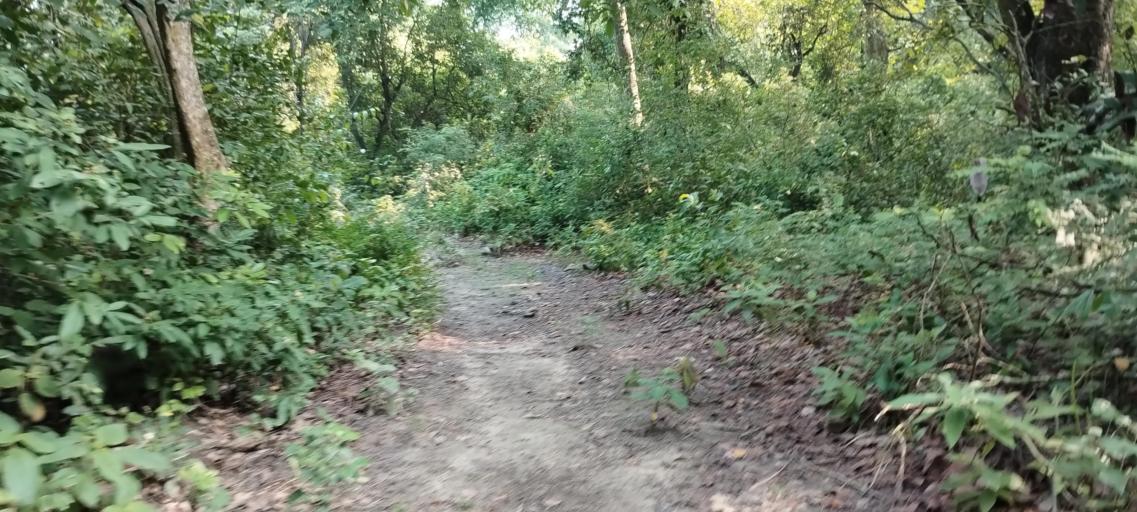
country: NP
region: Far Western
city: Tikapur
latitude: 28.4659
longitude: 81.2467
